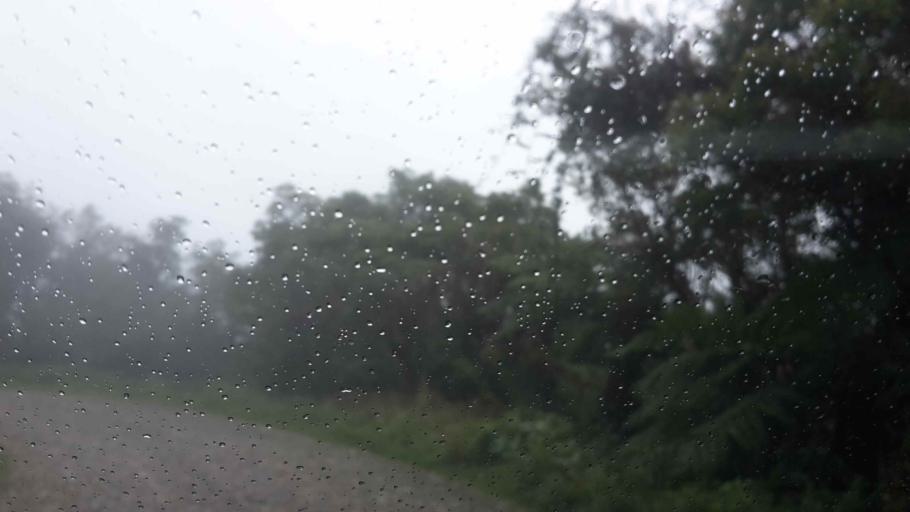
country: BO
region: Cochabamba
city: Colomi
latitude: -17.1683
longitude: -65.8954
